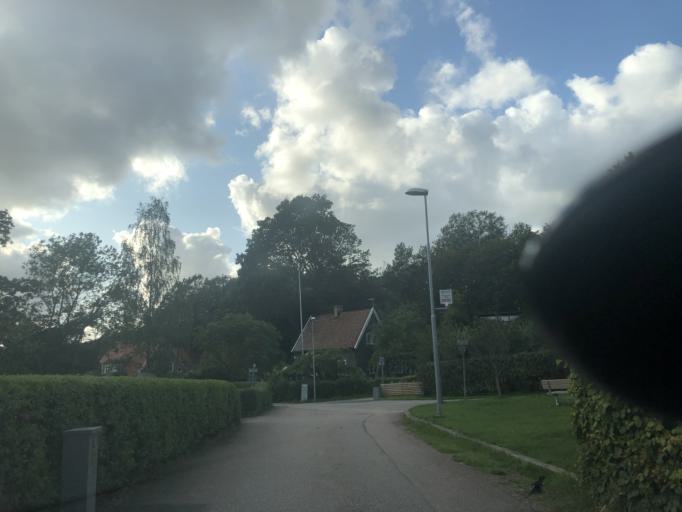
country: SE
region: Vaestra Goetaland
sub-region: Goteborg
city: Goeteborg
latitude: 57.7442
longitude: 11.9584
